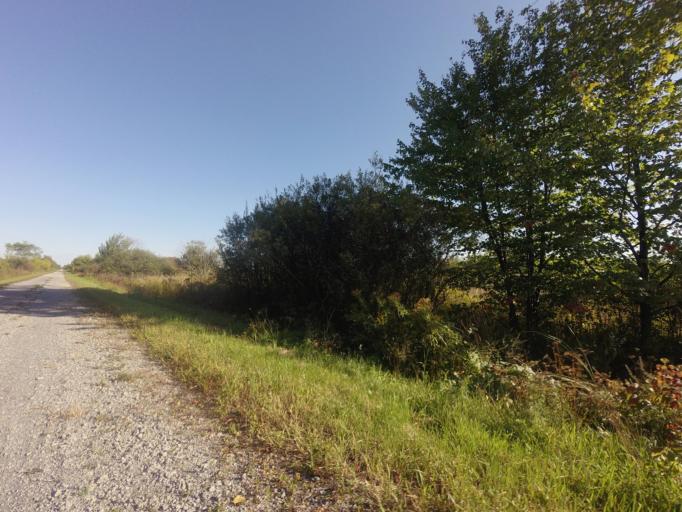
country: CA
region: Ontario
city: Hawkesbury
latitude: 45.5346
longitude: -74.5917
